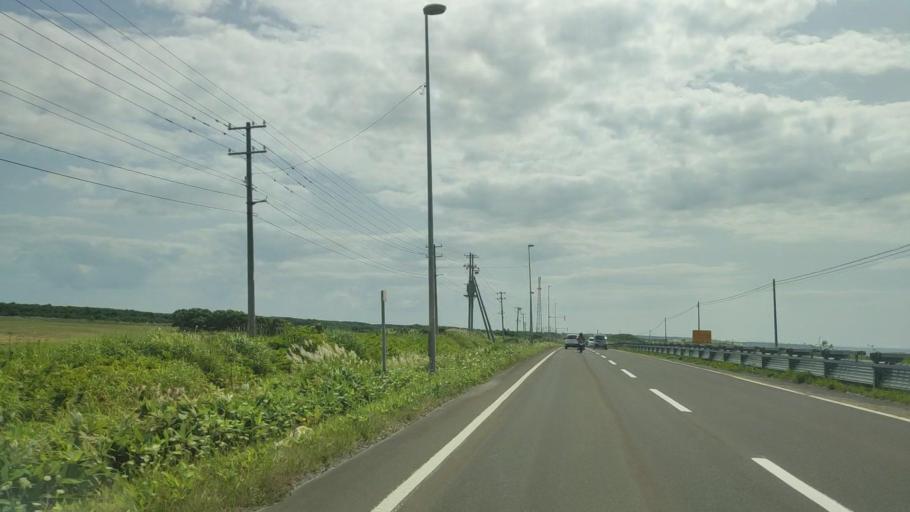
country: JP
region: Hokkaido
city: Rumoi
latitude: 44.4415
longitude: 141.7532
